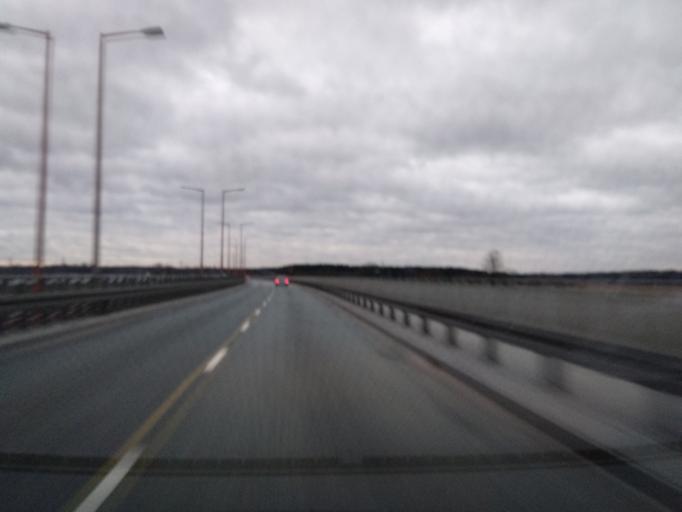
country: PL
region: Greater Poland Voivodeship
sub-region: Konin
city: Konin
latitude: 52.2210
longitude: 18.2349
